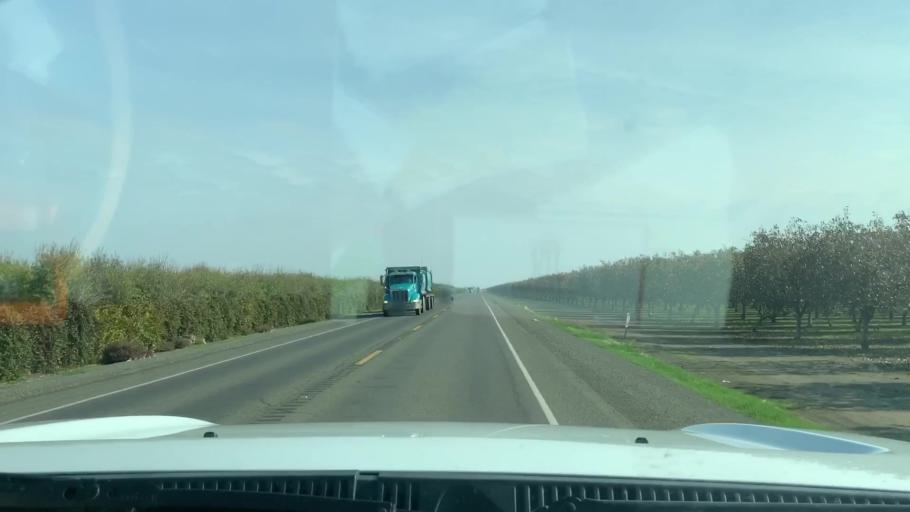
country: US
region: California
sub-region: Fresno County
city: Huron
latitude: 36.2553
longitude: -120.1162
